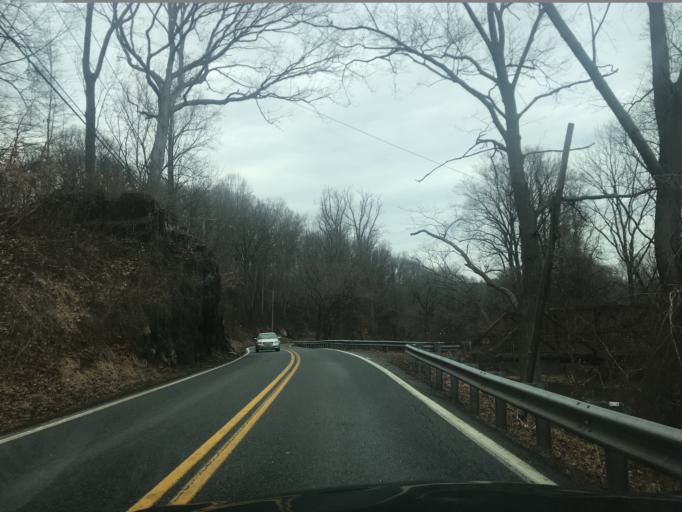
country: US
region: Maryland
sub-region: Harford County
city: Bel Air North
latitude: 39.6232
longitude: -76.4011
